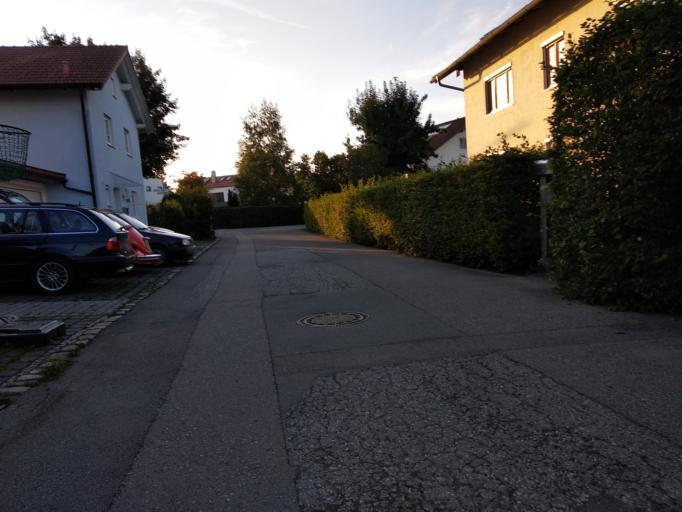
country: DE
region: Bavaria
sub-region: Upper Bavaria
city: Steinhoring
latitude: 48.0890
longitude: 12.0306
